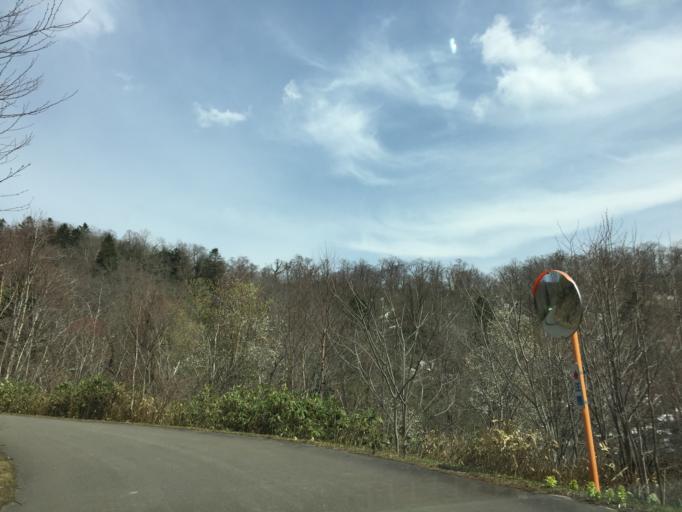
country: JP
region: Hokkaido
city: Akabira
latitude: 43.5997
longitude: 142.0647
